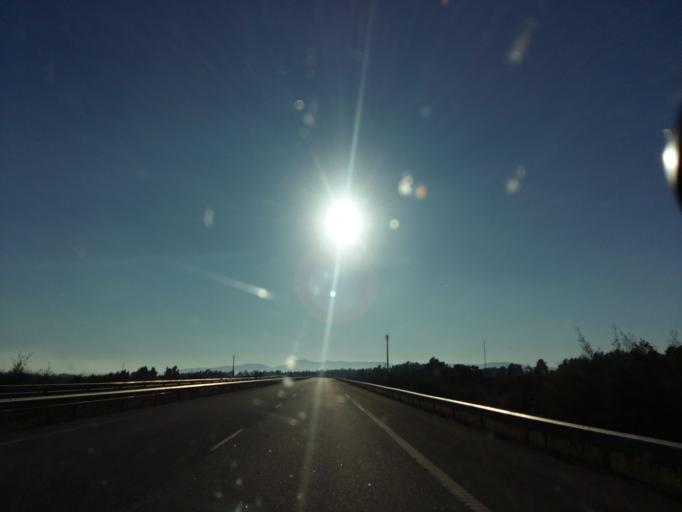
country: PT
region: Castelo Branco
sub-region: Castelo Branco
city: Castelo Branco
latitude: 39.7469
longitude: -7.6320
